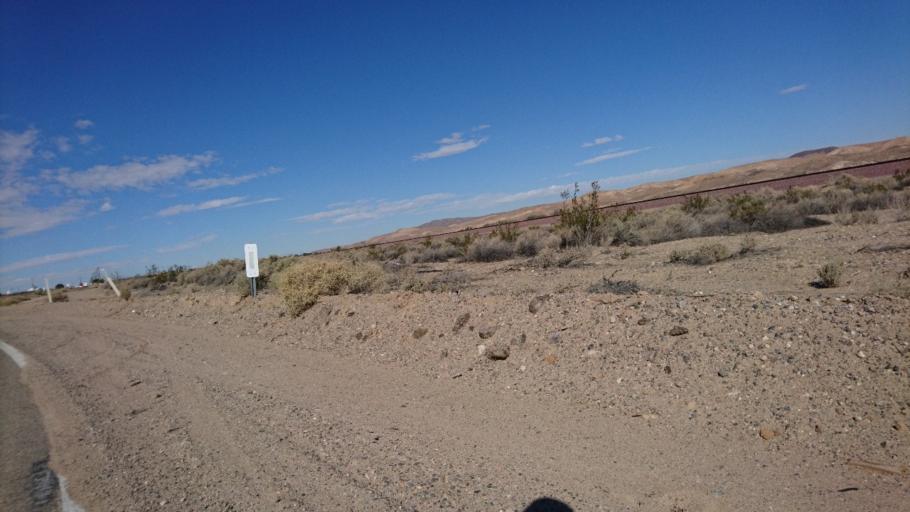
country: US
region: California
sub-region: San Bernardino County
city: Barstow
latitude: 34.8678
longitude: -116.9296
